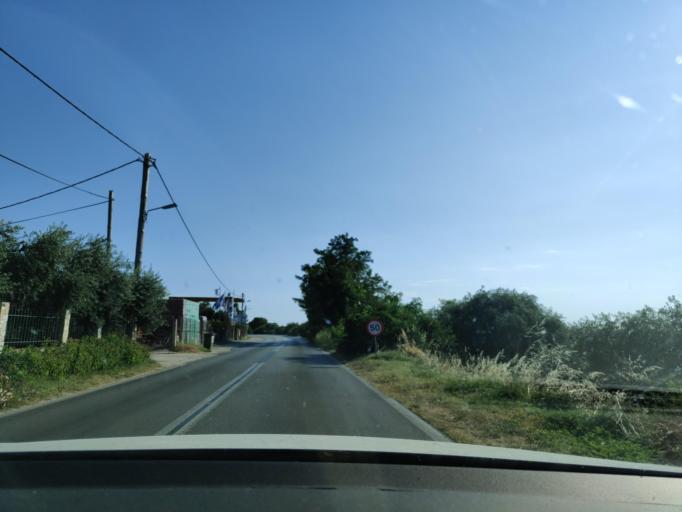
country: GR
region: East Macedonia and Thrace
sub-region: Nomos Kavalas
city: Prinos
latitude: 40.7152
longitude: 24.5357
